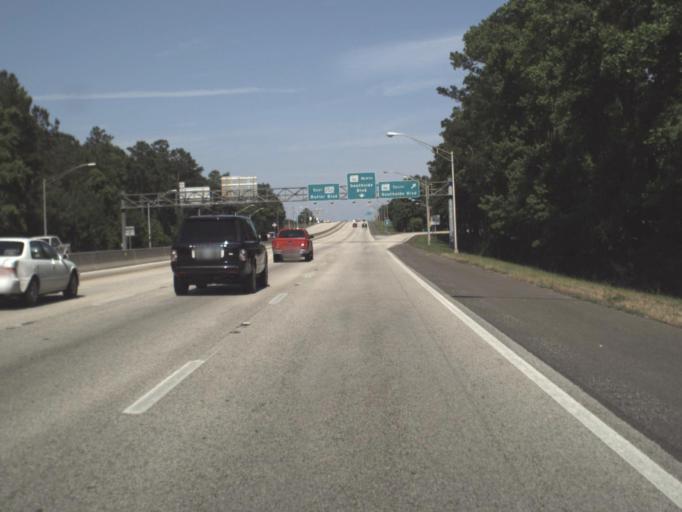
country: US
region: Florida
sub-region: Duval County
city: Jacksonville
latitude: 30.2499
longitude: -81.5598
